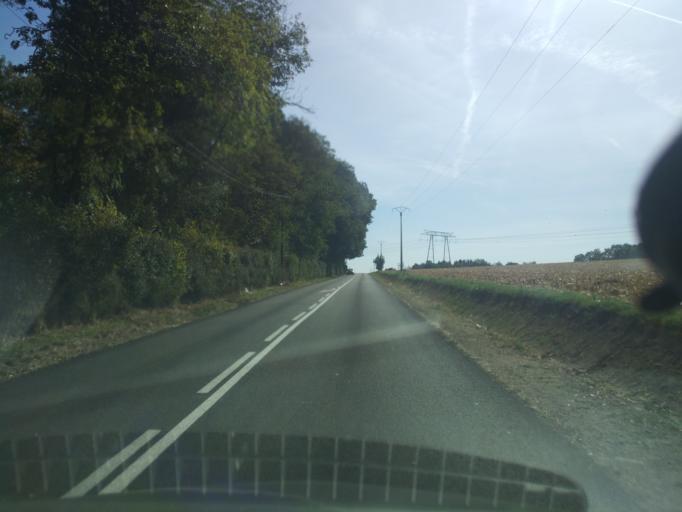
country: FR
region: Ile-de-France
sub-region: Departement de l'Essonne
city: Forges-les-Bains
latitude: 48.6388
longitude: 2.1022
